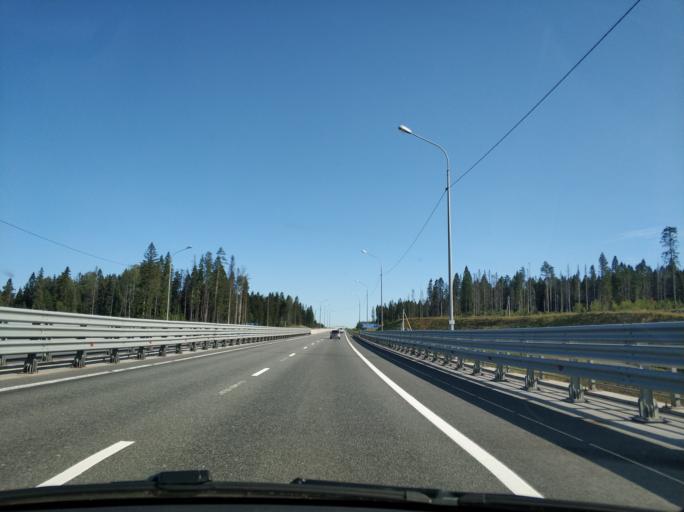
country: RU
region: Leningrad
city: Sosnovo
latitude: 60.4596
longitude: 30.1963
